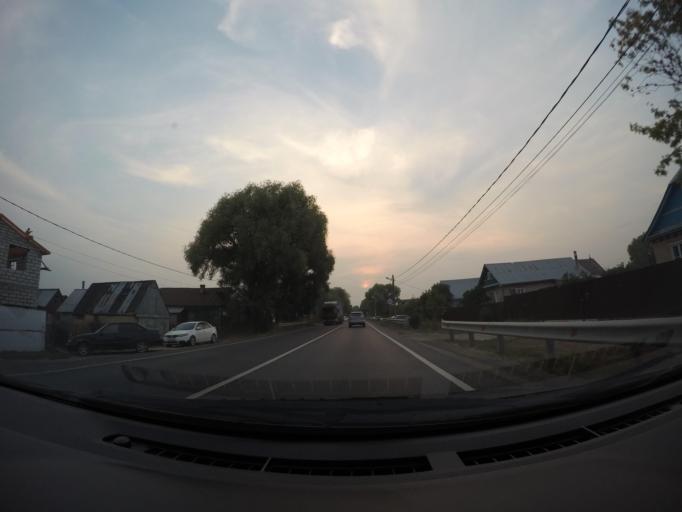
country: RU
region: Moskovskaya
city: Imeni Tsyurupy
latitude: 55.5762
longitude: 38.5890
